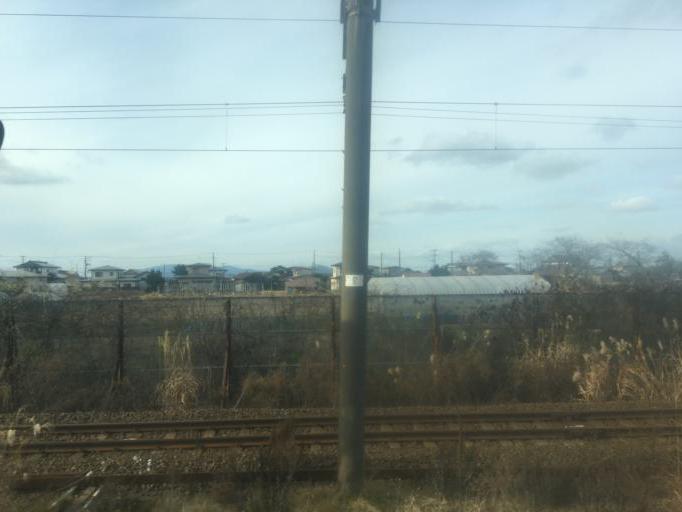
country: JP
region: Akita
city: Tenno
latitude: 39.8977
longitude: 140.0728
